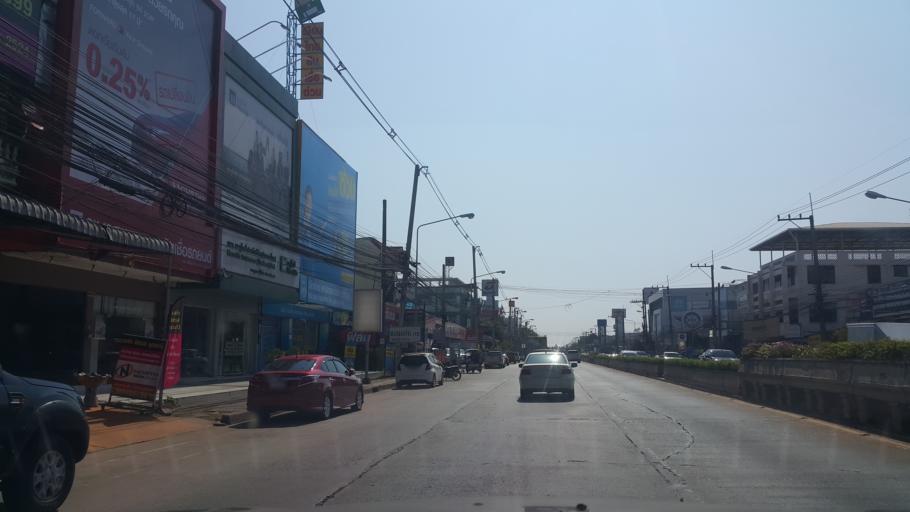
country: TH
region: Changwat Udon Thani
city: Udon Thani
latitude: 17.3927
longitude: 102.7990
